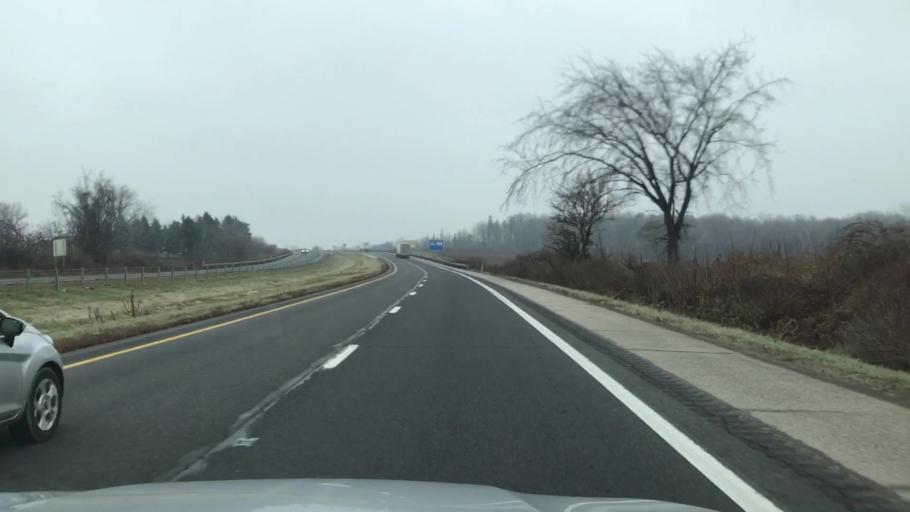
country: US
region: Pennsylvania
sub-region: Erie County
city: North East
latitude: 42.2245
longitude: -79.7845
